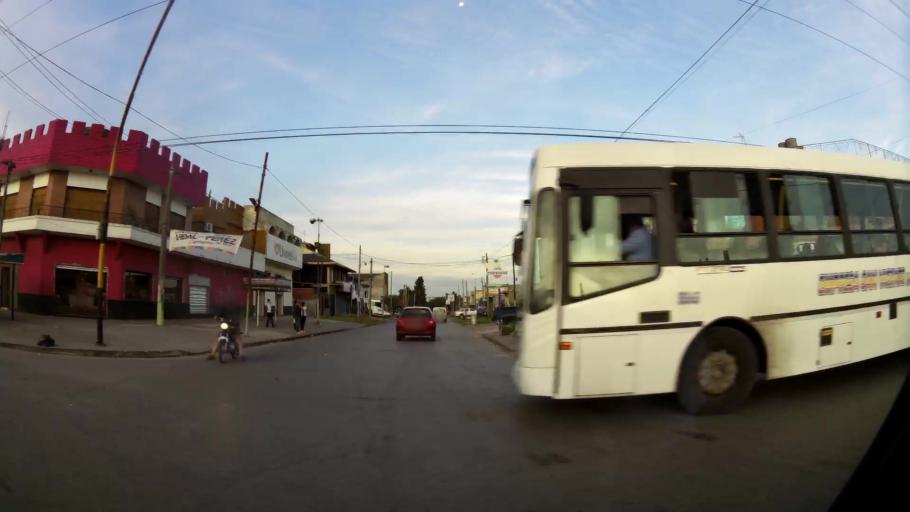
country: AR
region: Buenos Aires
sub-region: Partido de Almirante Brown
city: Adrogue
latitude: -34.7851
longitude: -58.3158
